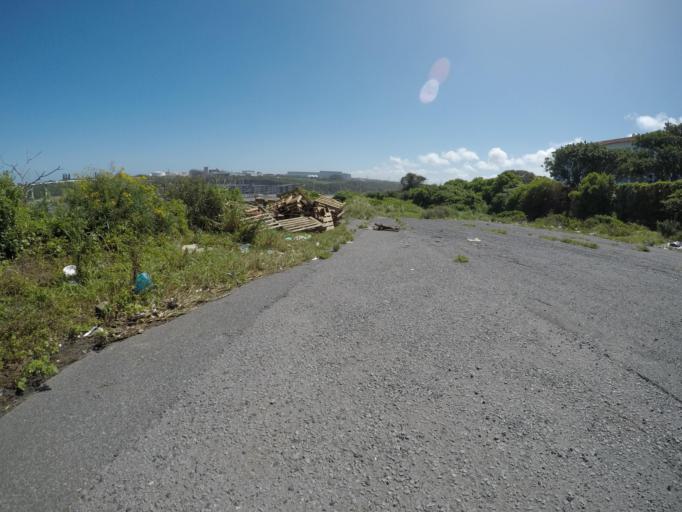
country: ZA
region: Eastern Cape
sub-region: Buffalo City Metropolitan Municipality
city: East London
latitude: -33.0228
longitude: 27.9061
